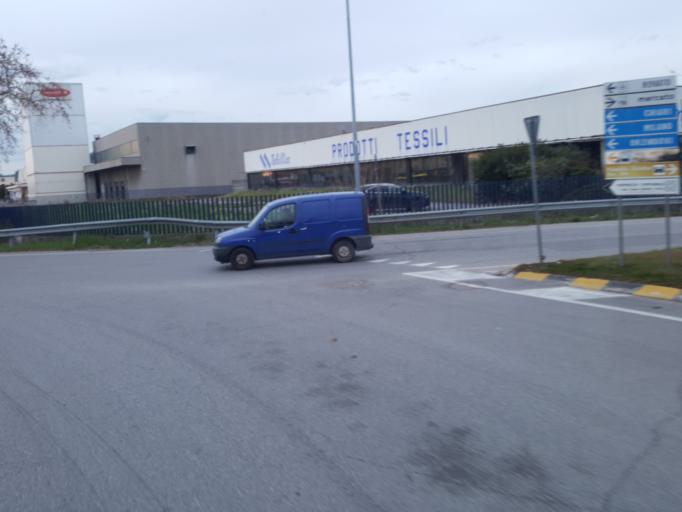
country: IT
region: Lombardy
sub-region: Provincia di Brescia
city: Rovato
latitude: 45.5604
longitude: 10.0137
